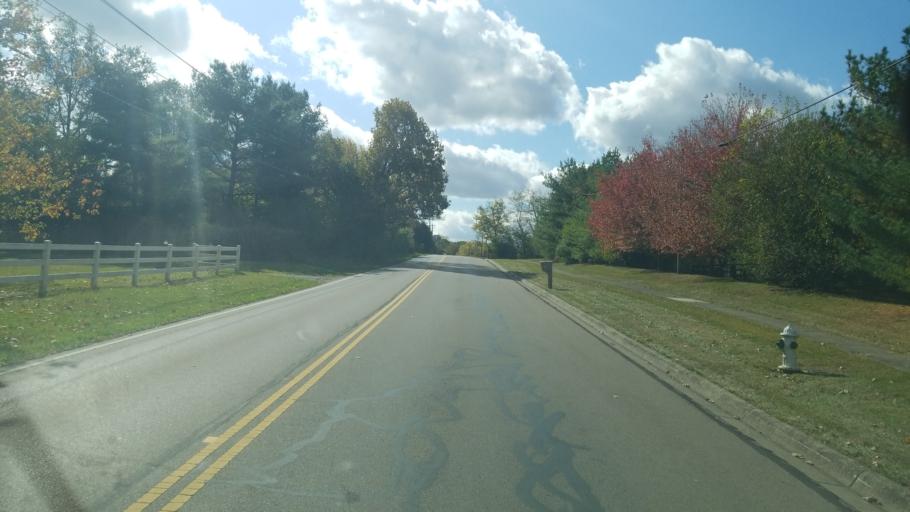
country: US
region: Ohio
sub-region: Warren County
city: Lebanon
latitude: 39.4270
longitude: -84.1879
